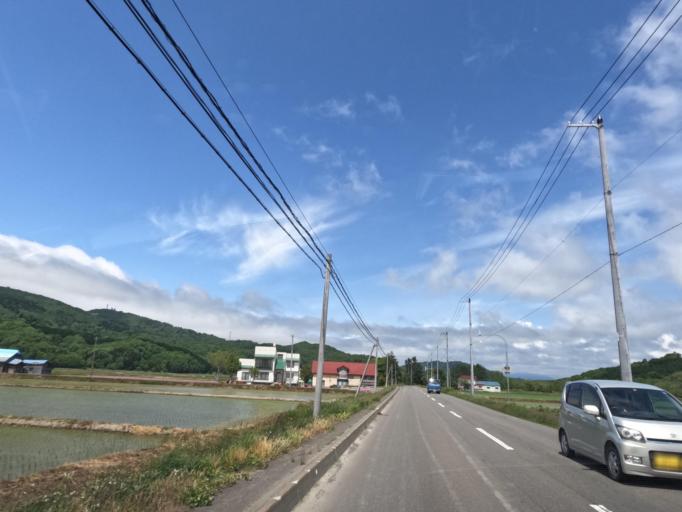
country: JP
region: Hokkaido
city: Tobetsu
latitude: 43.2853
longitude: 141.5372
